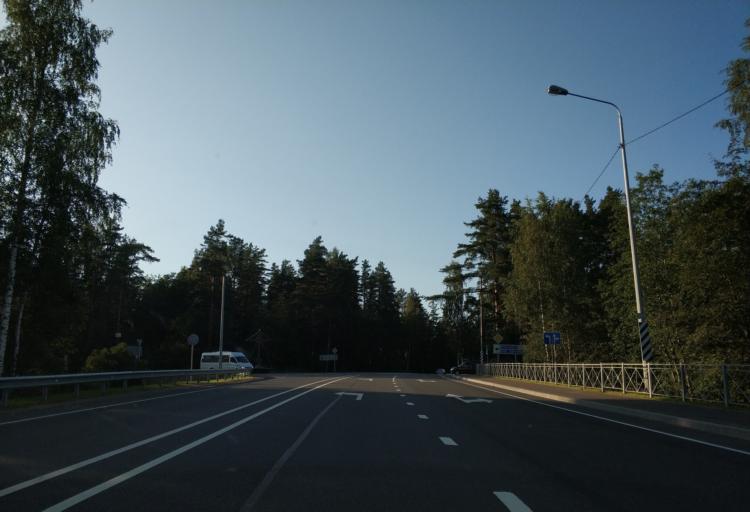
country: RU
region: Leningrad
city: Sapernoye
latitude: 60.7054
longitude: 29.9686
